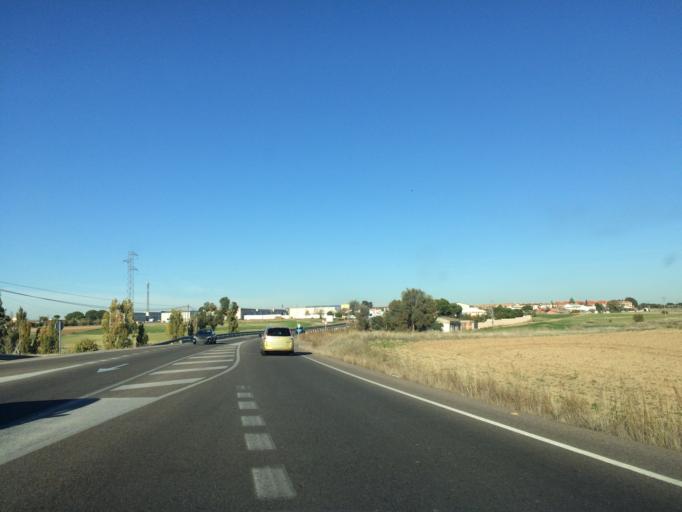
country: ES
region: Castille-La Mancha
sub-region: Province of Toledo
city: Carranque
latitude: 40.1776
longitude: -3.8902
